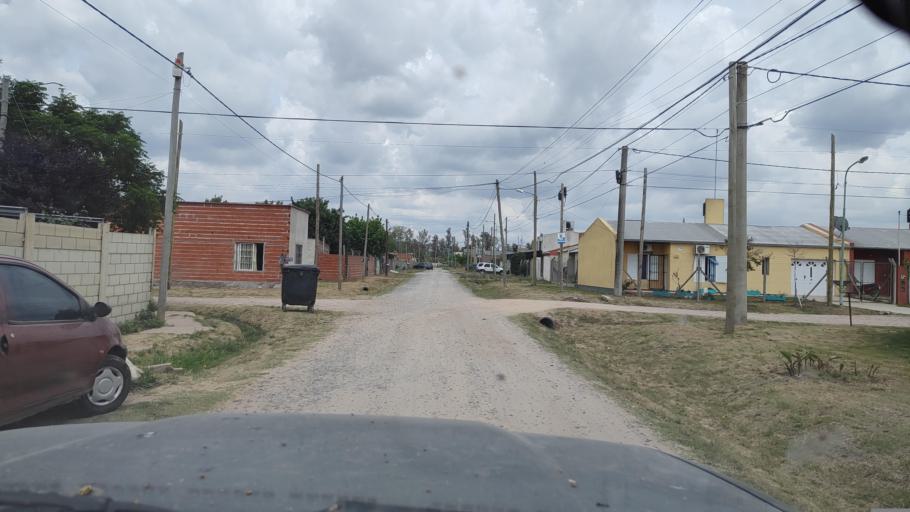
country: AR
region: Buenos Aires
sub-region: Partido de Lujan
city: Lujan
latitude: -34.5549
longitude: -59.1355
